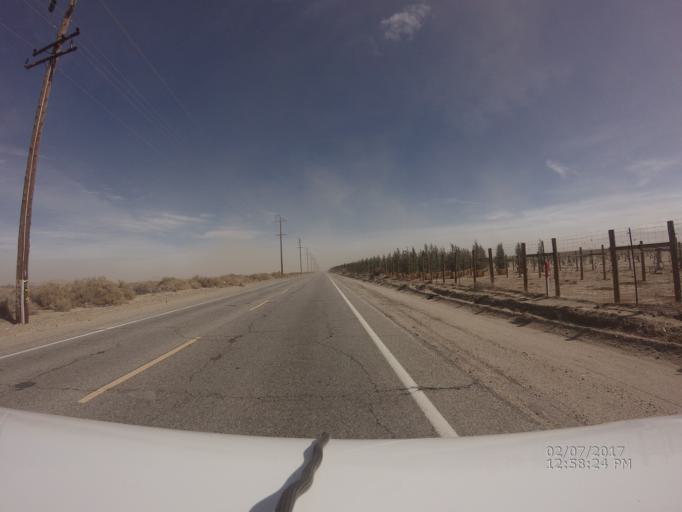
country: US
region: California
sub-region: Los Angeles County
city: Lake Los Angeles
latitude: 34.5798
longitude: -117.8432
